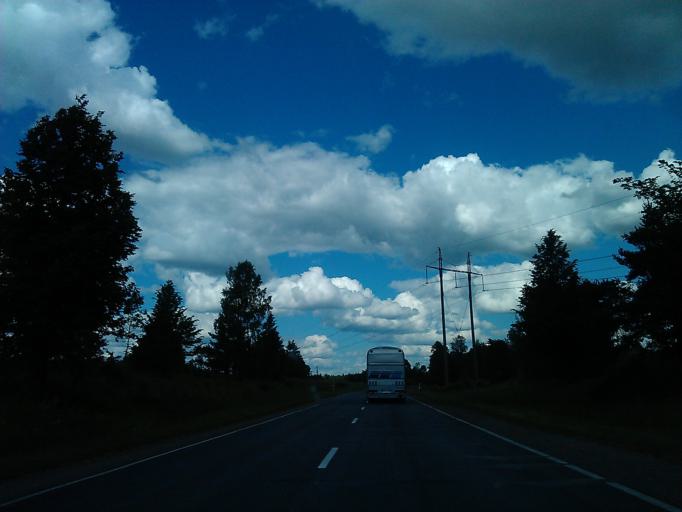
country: LV
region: Rezekne
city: Rezekne
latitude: 56.5441
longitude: 27.3062
